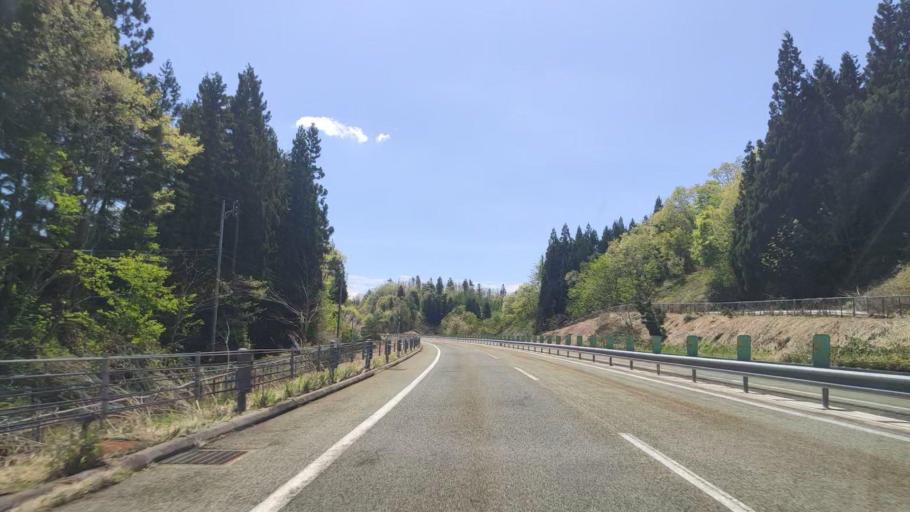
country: JP
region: Akita
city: Yokotemachi
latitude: 39.2867
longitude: 140.5295
